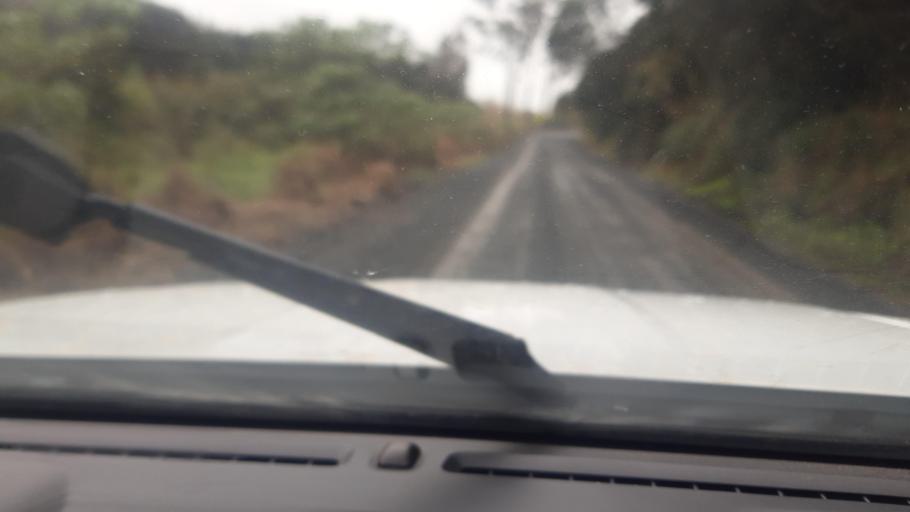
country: NZ
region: Northland
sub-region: Far North District
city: Kaitaia
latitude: -34.9944
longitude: 173.2172
